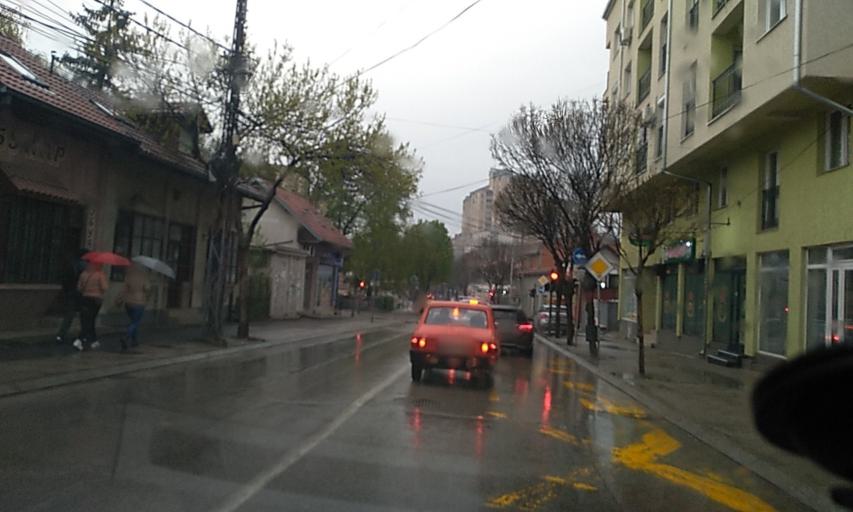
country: RS
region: Central Serbia
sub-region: Nisavski Okrug
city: Nis
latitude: 43.3116
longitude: 21.8936
